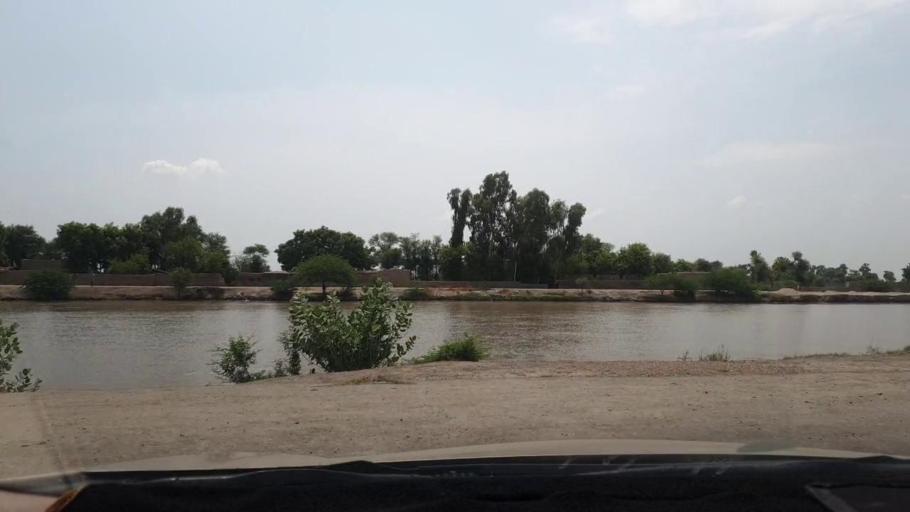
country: PK
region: Sindh
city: Naudero
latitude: 27.6577
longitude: 68.3321
